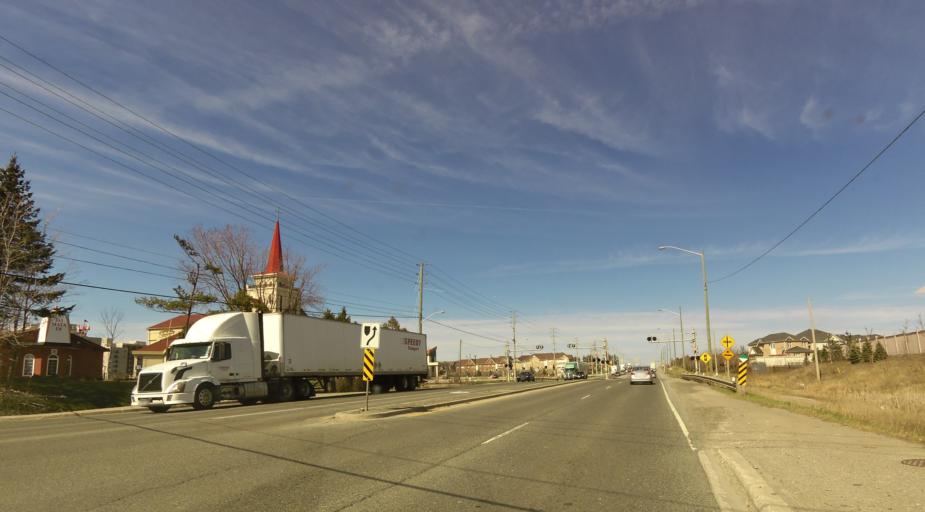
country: CA
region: Ontario
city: Brampton
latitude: 43.6401
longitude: -79.7618
